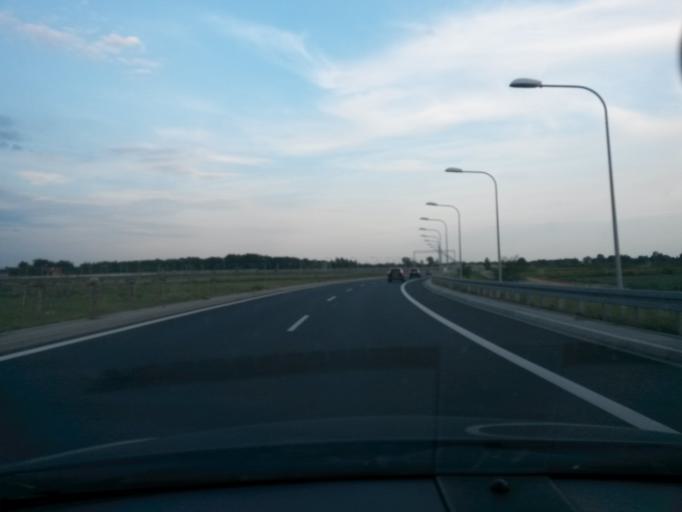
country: PL
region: Masovian Voivodeship
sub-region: Powiat pruszkowski
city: Rybie
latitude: 52.1383
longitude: 20.9835
